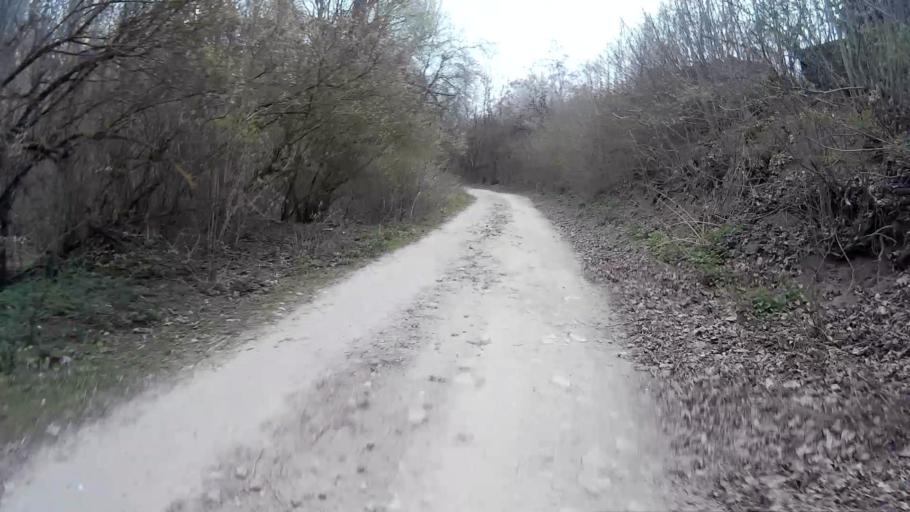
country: CZ
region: South Moravian
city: Ivancice
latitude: 49.0893
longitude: 16.3509
